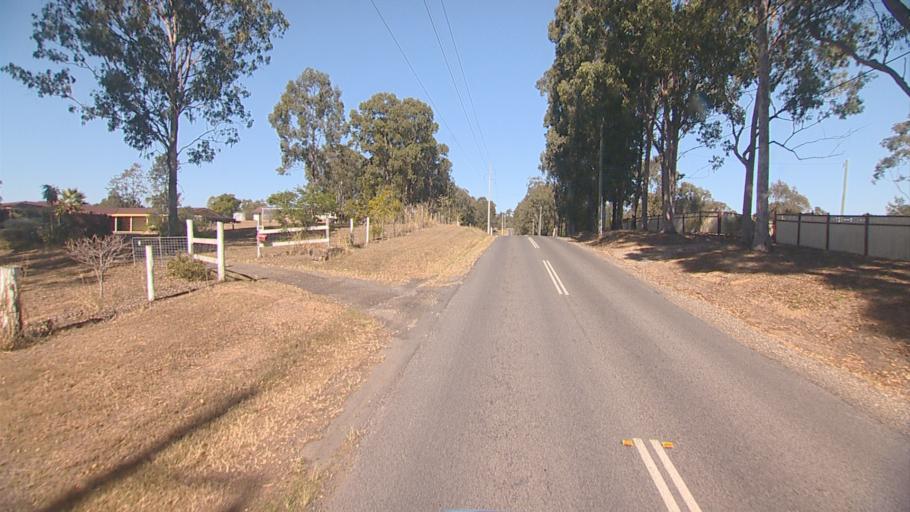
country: AU
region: Queensland
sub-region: Logan
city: Cedar Vale
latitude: -27.8767
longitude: 153.0164
